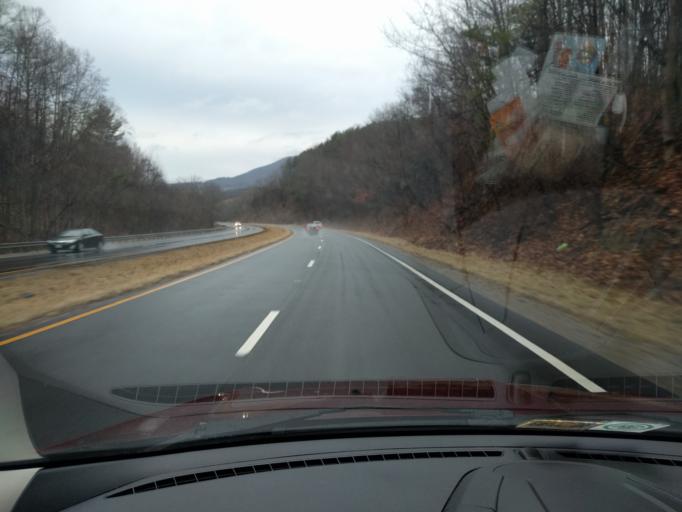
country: US
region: Virginia
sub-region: Montgomery County
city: Prices Fork
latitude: 37.3050
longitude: -80.5087
